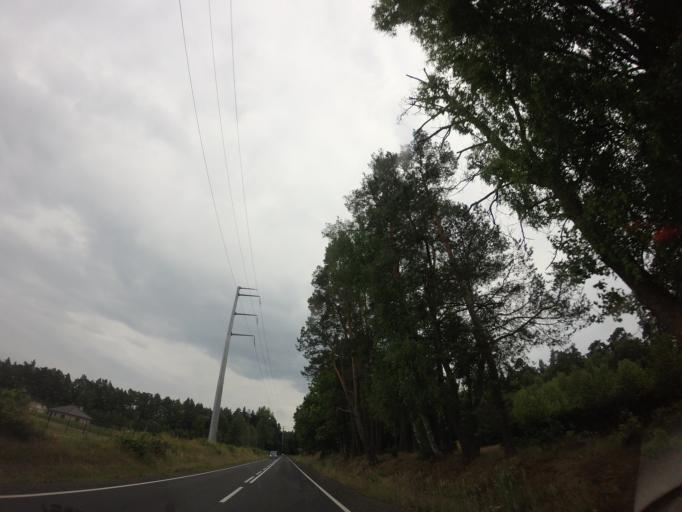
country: PL
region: West Pomeranian Voivodeship
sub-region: Powiat drawski
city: Czaplinek
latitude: 53.5081
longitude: 16.2230
